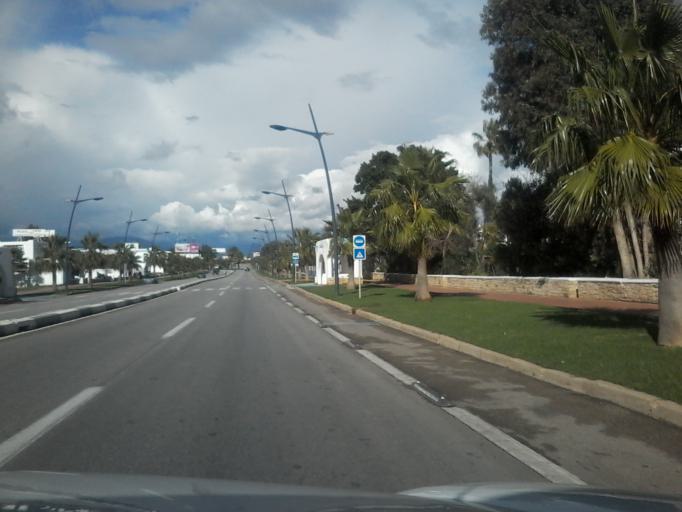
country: MA
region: Tanger-Tetouan
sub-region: Tetouan
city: Martil
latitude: 35.7313
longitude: -5.3410
